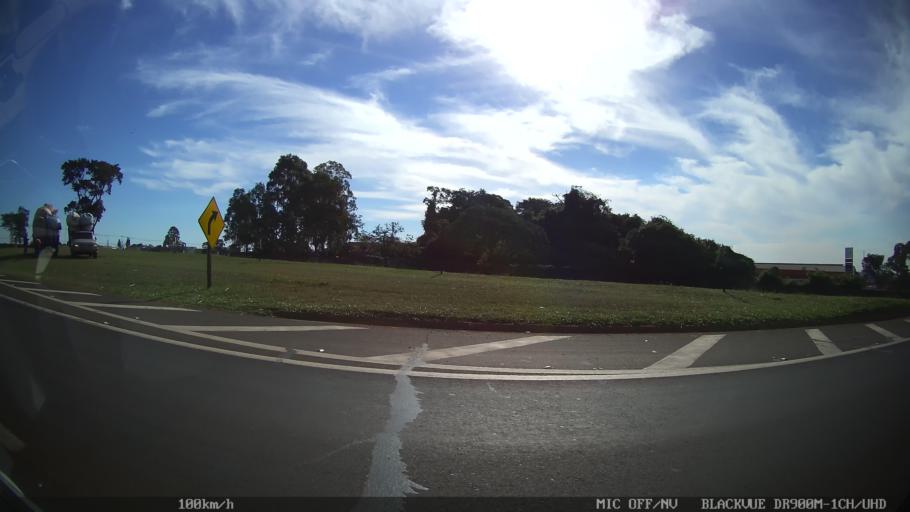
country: BR
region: Sao Paulo
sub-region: Araraquara
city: Araraquara
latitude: -21.8122
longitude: -48.1566
